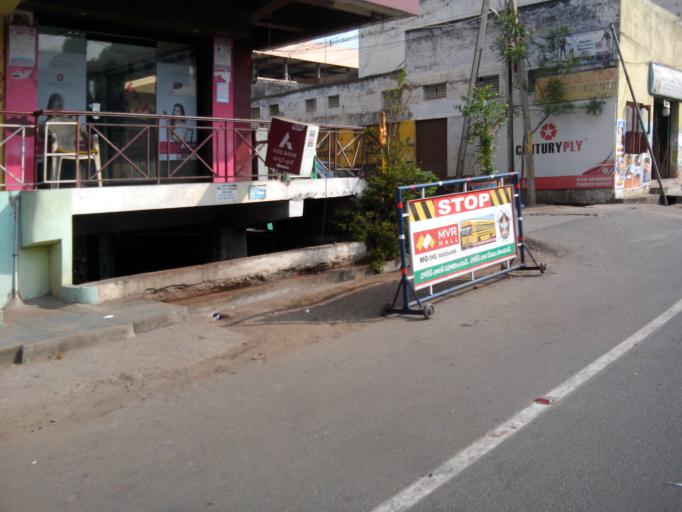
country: IN
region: Andhra Pradesh
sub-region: Krishna
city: Vijayawada
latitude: 16.5162
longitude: 80.6404
